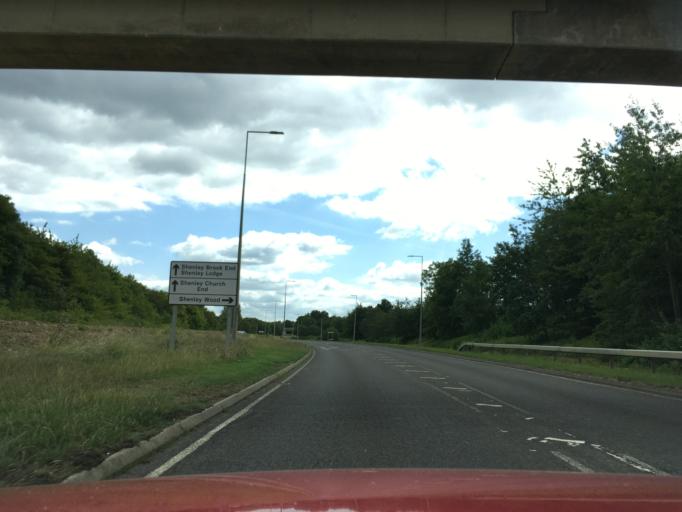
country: GB
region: England
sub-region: Milton Keynes
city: Shenley Church End
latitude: 52.0188
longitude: -0.7934
